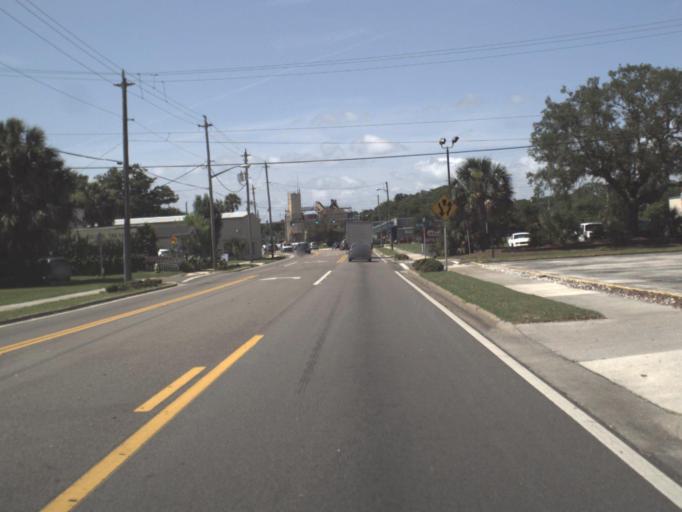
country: US
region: Florida
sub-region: Nassau County
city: Fernandina Beach
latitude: 30.6575
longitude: -81.4609
